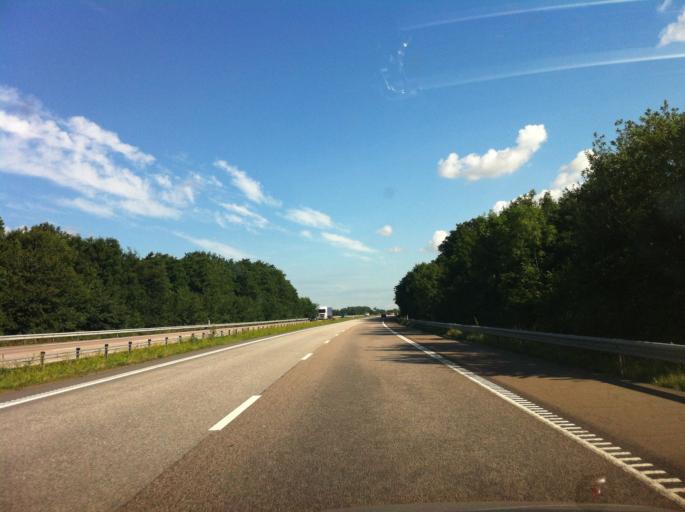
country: SE
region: Skane
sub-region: Angelholms Kommun
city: Strovelstorp
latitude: 56.1581
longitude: 12.8438
